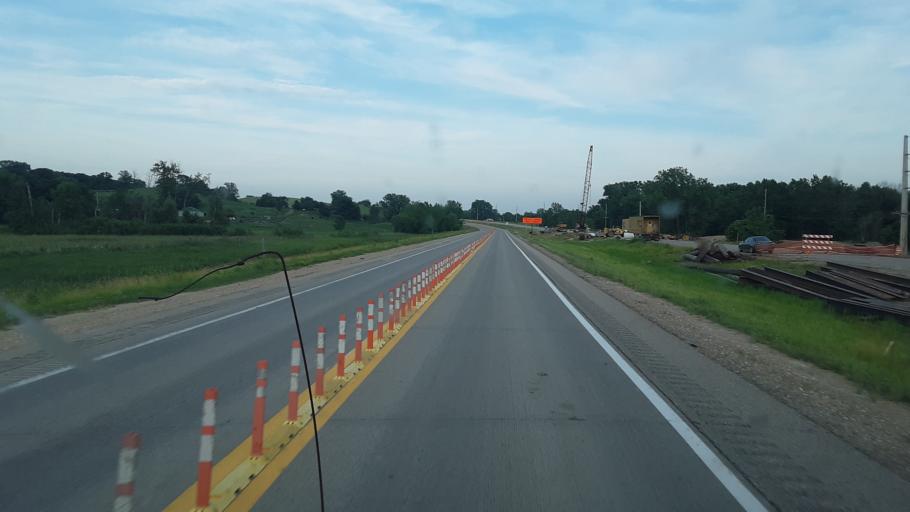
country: US
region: Iowa
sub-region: Tama County
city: Toledo
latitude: 42.0010
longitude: -92.7062
